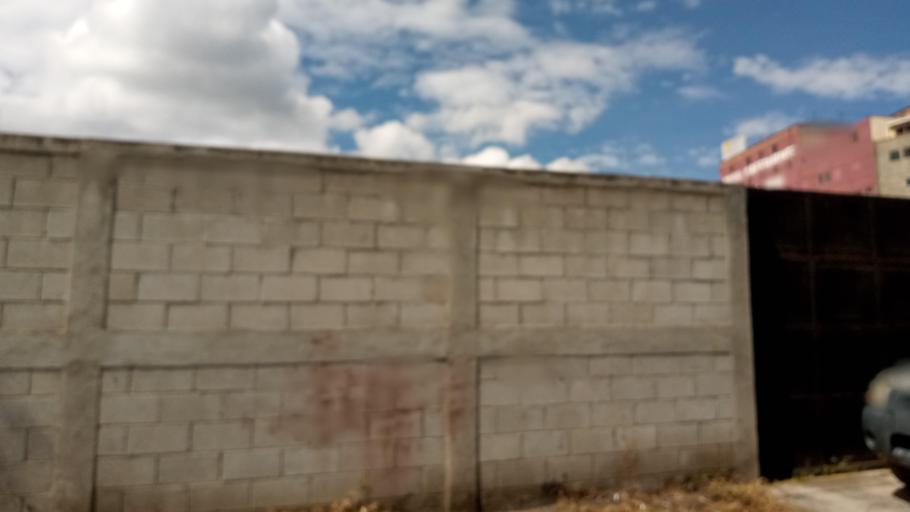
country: GT
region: Quetzaltenango
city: Quetzaltenango
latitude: 14.8429
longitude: -91.5115
